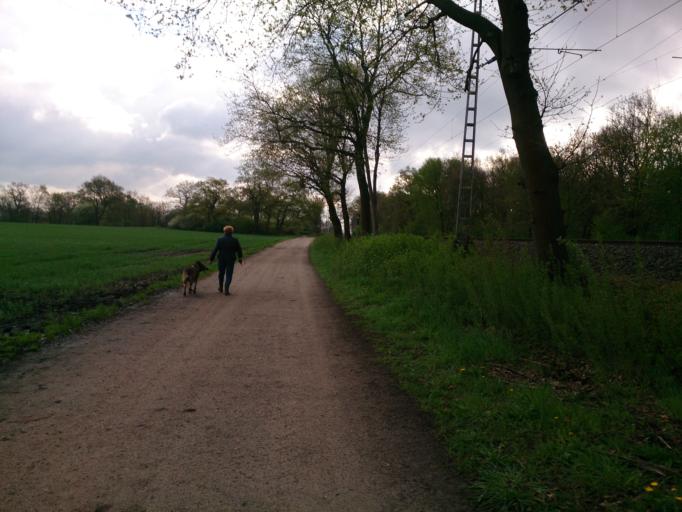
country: DE
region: Lower Saxony
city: Neu Wulmstorf
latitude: 53.4751
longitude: 9.8244
